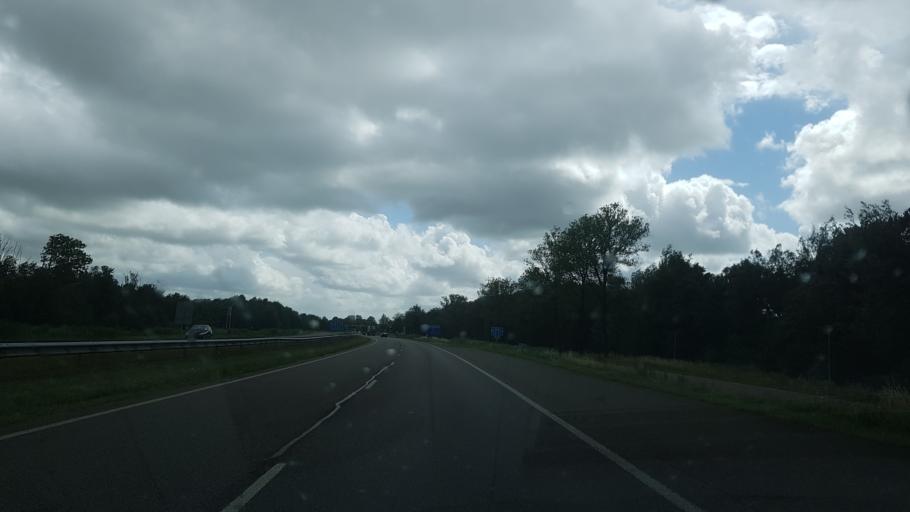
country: NL
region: Friesland
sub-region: Gemeente Leeuwarden
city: Camminghaburen
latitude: 53.2168
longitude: 5.8581
